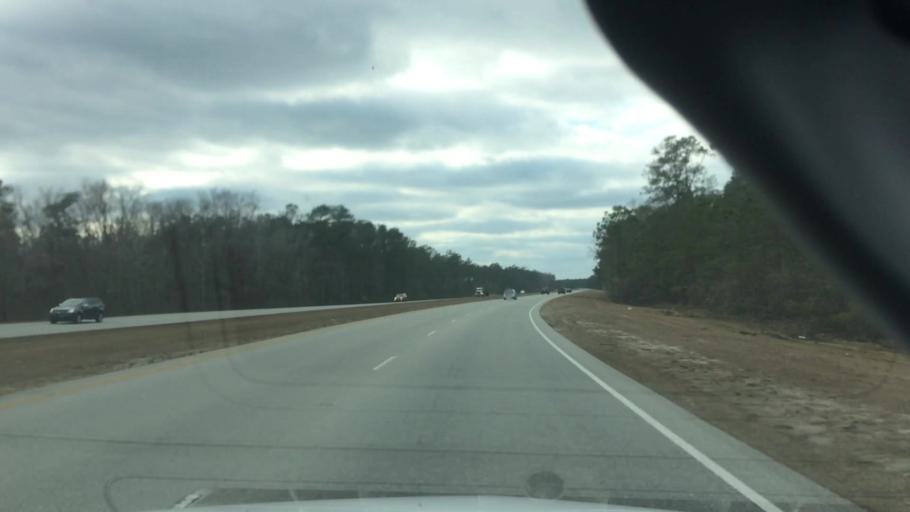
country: US
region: North Carolina
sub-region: Brunswick County
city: Bolivia
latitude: 34.0783
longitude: -78.1444
